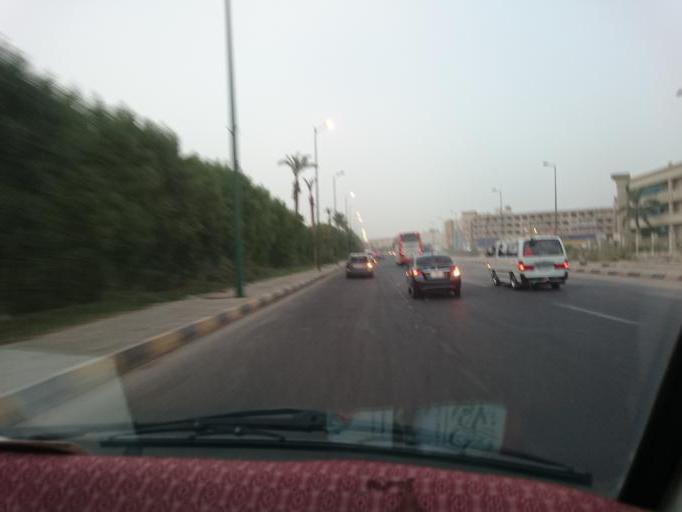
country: EG
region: Red Sea
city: Hurghada
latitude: 27.1982
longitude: 33.8221
